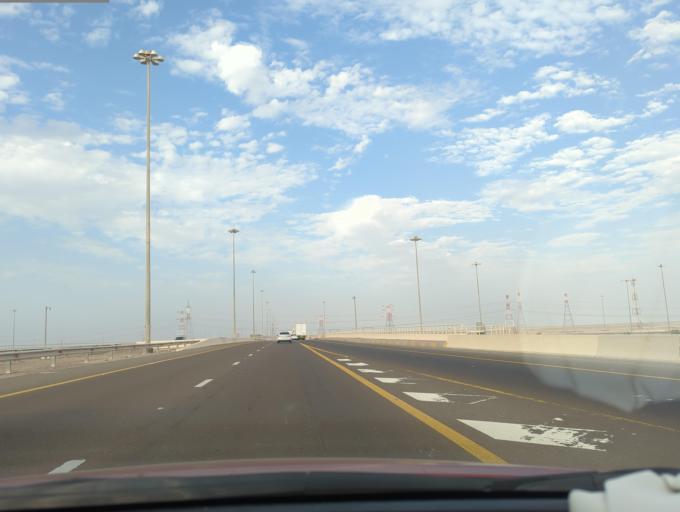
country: AE
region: Abu Dhabi
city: Abu Dhabi
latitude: 24.4183
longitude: 54.7627
